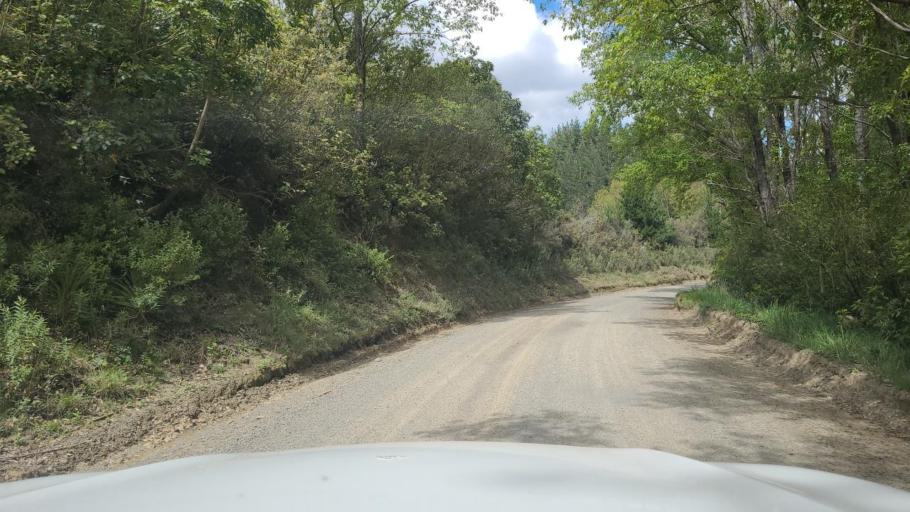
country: NZ
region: Hawke's Bay
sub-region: Napier City
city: Napier
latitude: -39.2510
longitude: 176.7316
